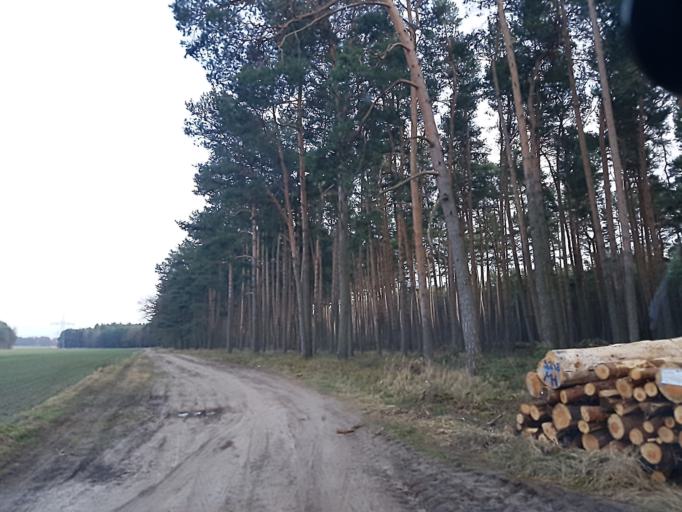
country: DE
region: Brandenburg
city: Wollin
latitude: 52.2644
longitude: 12.5104
